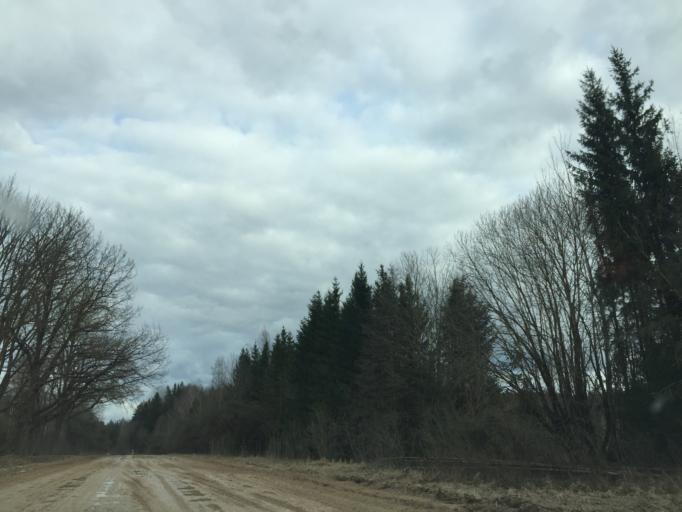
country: LV
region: Lielvarde
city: Lielvarde
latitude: 56.5265
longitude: 24.7743
